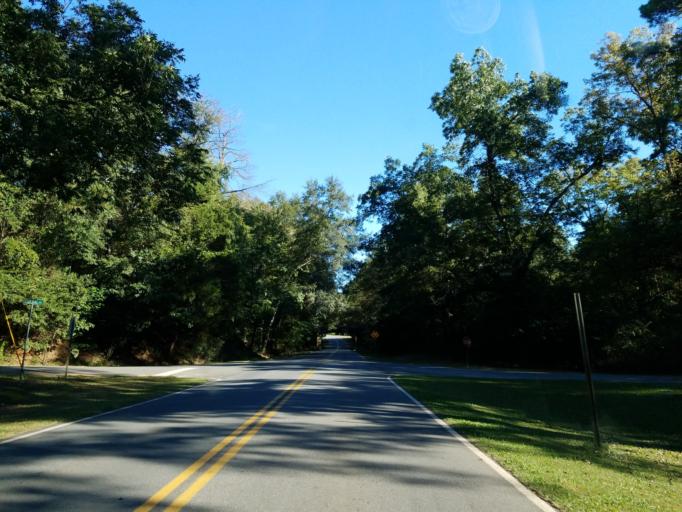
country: US
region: Georgia
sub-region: Dooly County
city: Vienna
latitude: 32.2004
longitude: -83.9076
